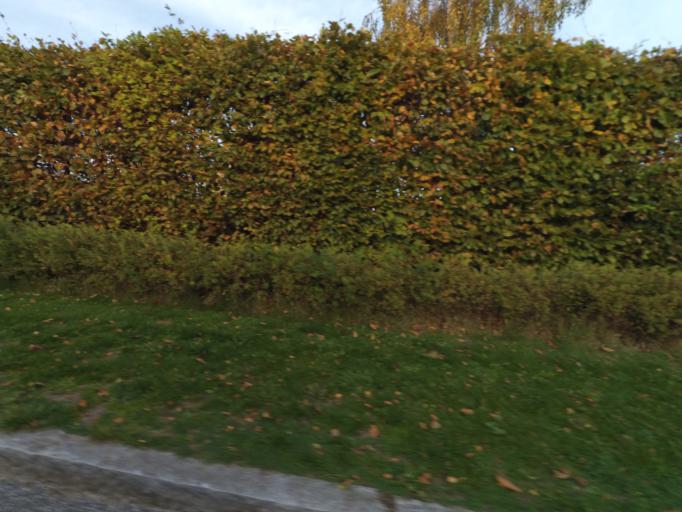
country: DK
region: Central Jutland
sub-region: Arhus Kommune
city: Stavtrup
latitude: 56.1605
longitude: 10.0982
